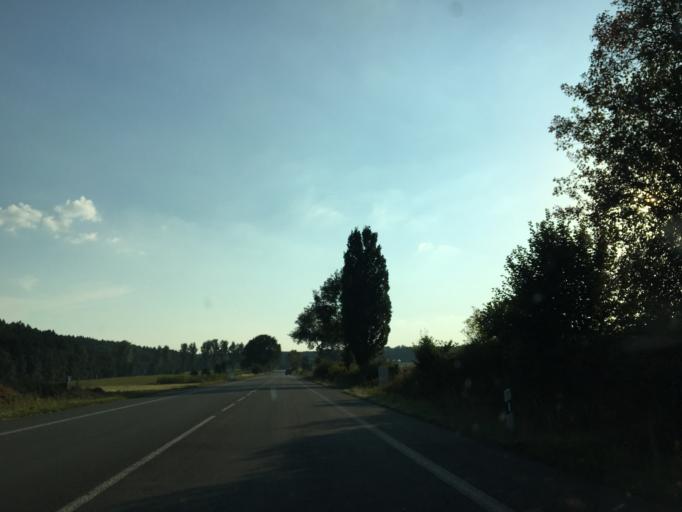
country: DE
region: Hesse
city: Frankenberg
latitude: 51.0171
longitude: 8.8027
